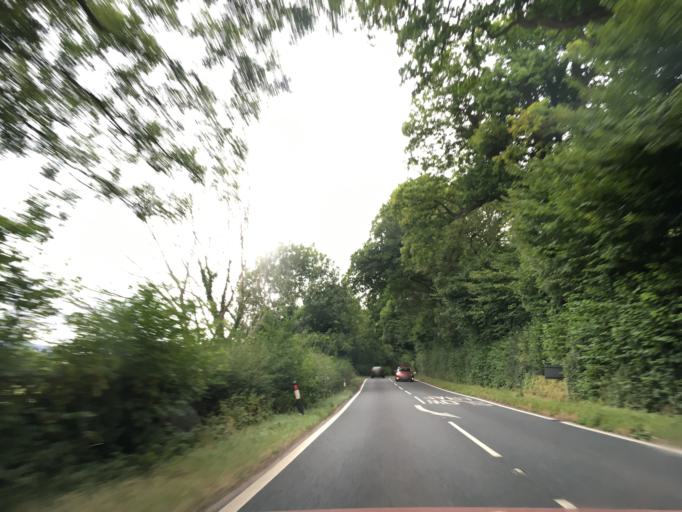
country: GB
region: Wales
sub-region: Sir Powys
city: Brecon
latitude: 51.9173
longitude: -3.3023
